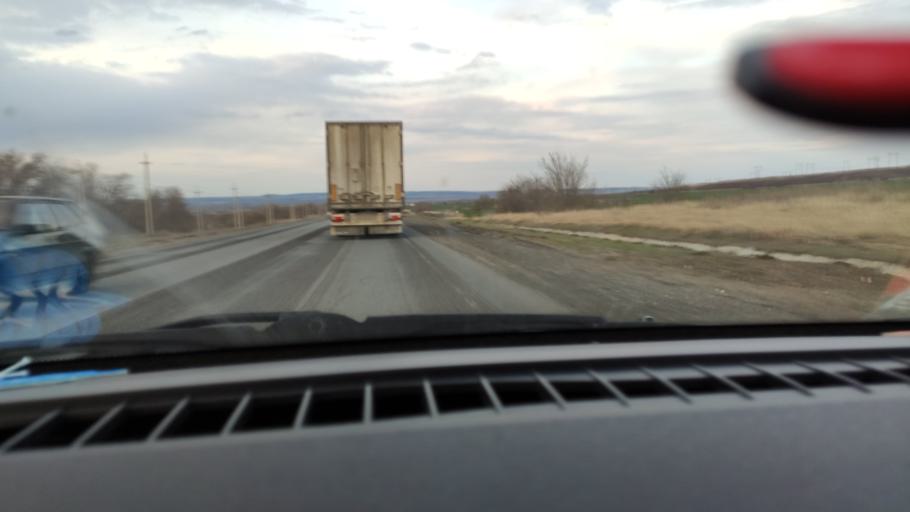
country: RU
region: Saratov
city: Shumeyka
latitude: 51.7888
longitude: 46.1462
